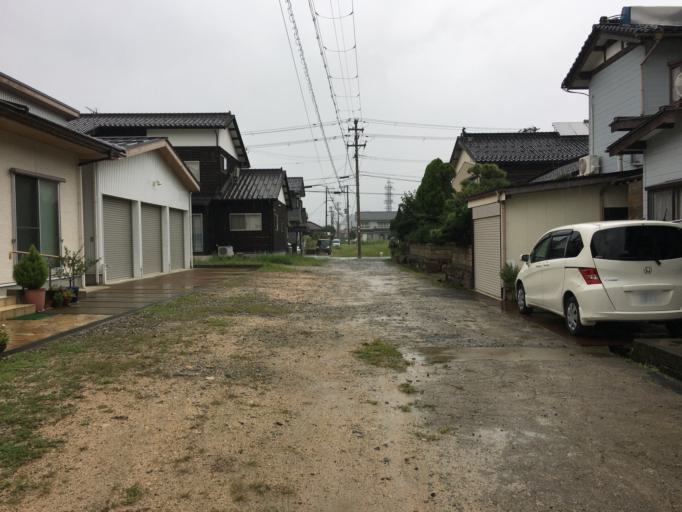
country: JP
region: Hyogo
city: Toyooka
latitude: 35.6330
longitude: 134.6277
